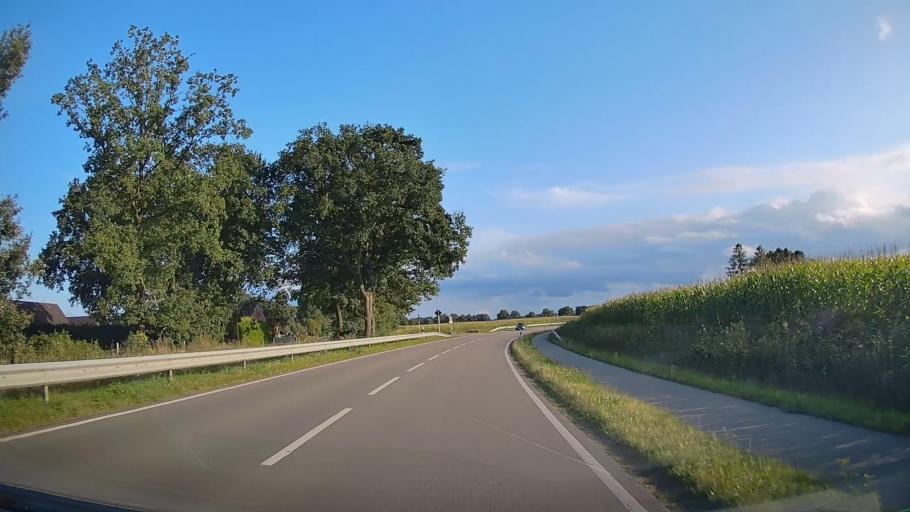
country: DE
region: Lower Saxony
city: Hilkenbrook
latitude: 53.0679
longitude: 7.7221
